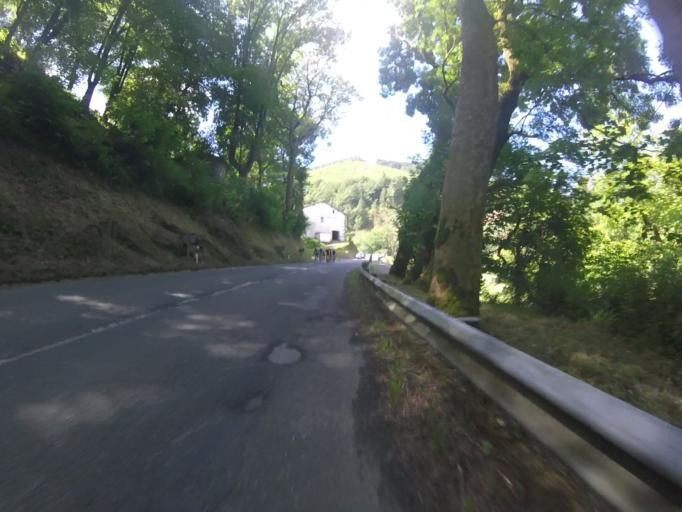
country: ES
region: Basque Country
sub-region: Provincia de Guipuzcoa
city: Azpeitia
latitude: 43.1799
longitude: -2.2250
